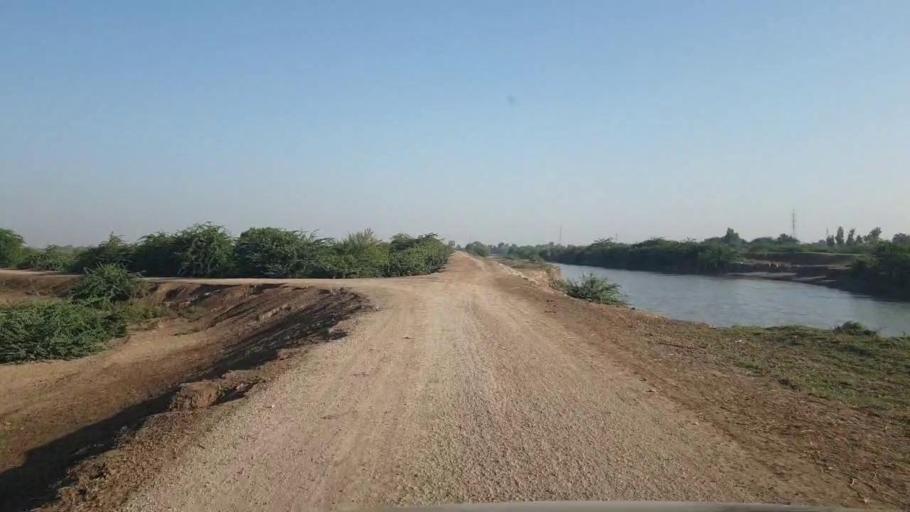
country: PK
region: Sindh
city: Badin
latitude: 24.6969
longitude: 68.8166
